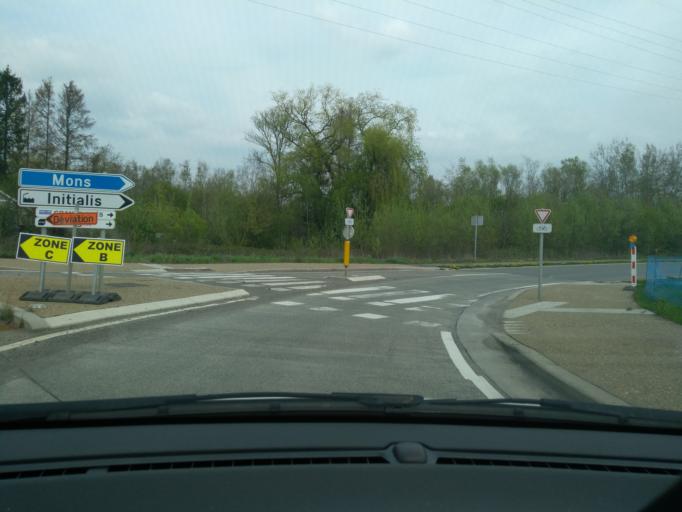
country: BE
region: Wallonia
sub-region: Province du Hainaut
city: Mons
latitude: 50.4565
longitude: 3.9233
